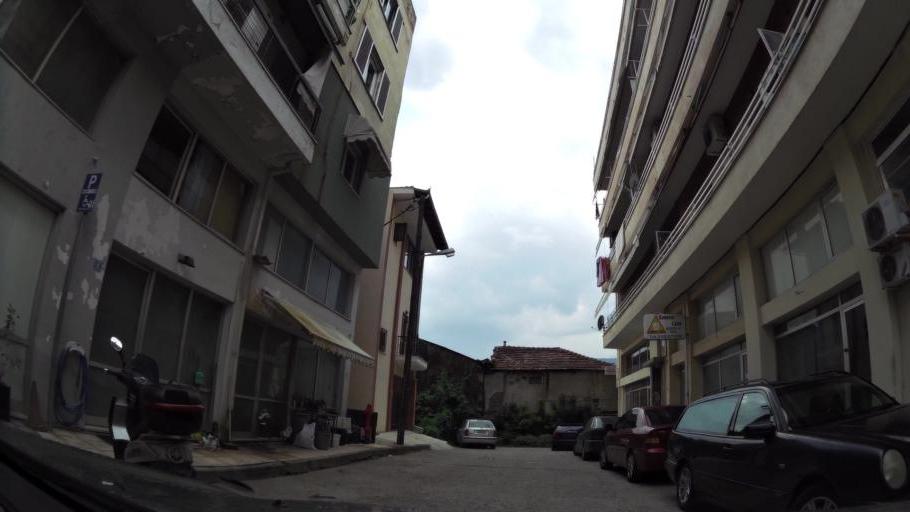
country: GR
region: Central Macedonia
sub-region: Nomos Imathias
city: Veroia
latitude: 40.5263
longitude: 22.2018
